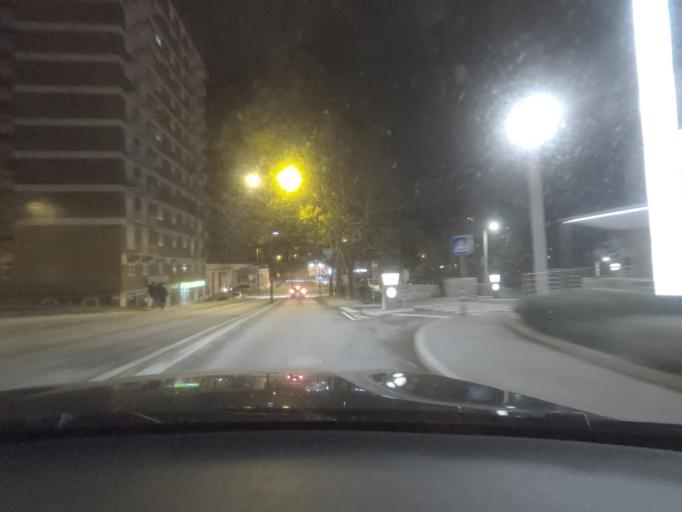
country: PT
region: Vila Real
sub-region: Vila Real
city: Vila Real
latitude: 41.2981
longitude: -7.7499
